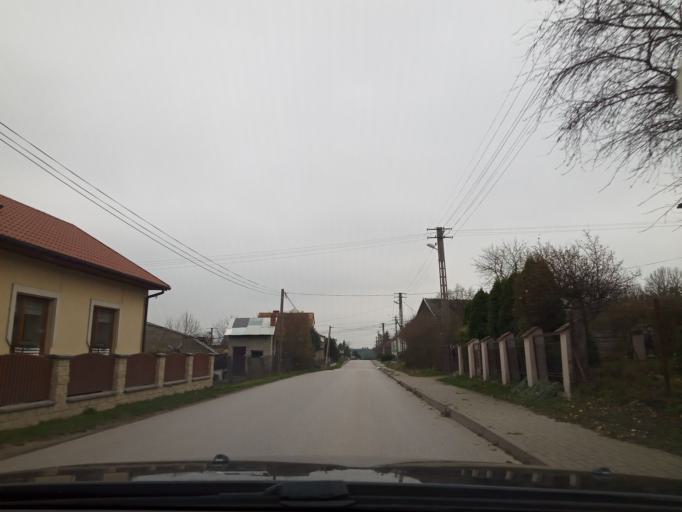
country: PL
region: Swietokrzyskie
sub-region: Powiat jedrzejowski
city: Imielno
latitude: 50.5865
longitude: 20.4454
